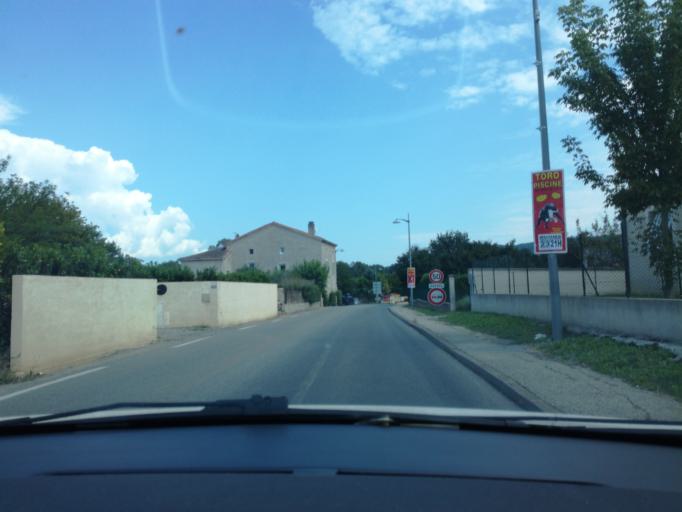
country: FR
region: Rhone-Alpes
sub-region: Departement de l'Ardeche
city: Ruoms
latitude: 44.4756
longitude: 4.3608
